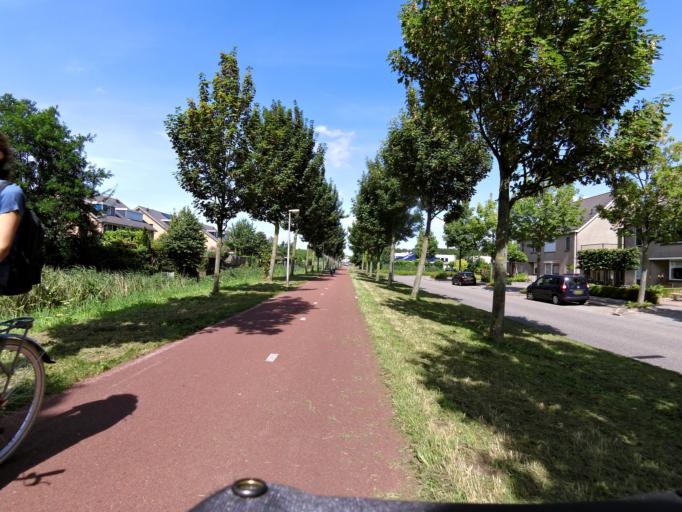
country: NL
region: South Holland
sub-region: Gemeente Barendrecht
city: Barendrecht
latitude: 51.8607
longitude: 4.5289
